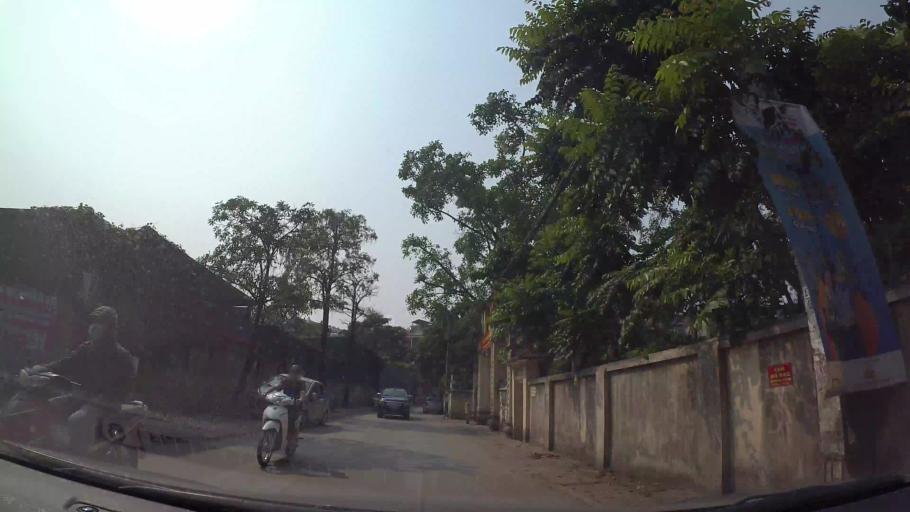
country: VN
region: Ha Noi
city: Thanh Xuan
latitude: 20.9841
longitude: 105.8201
